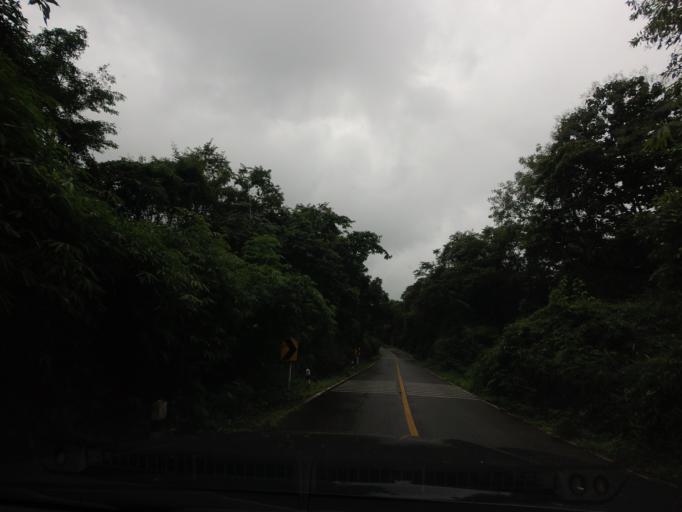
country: TH
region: Nong Khai
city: Sangkhom
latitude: 18.0268
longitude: 102.3487
